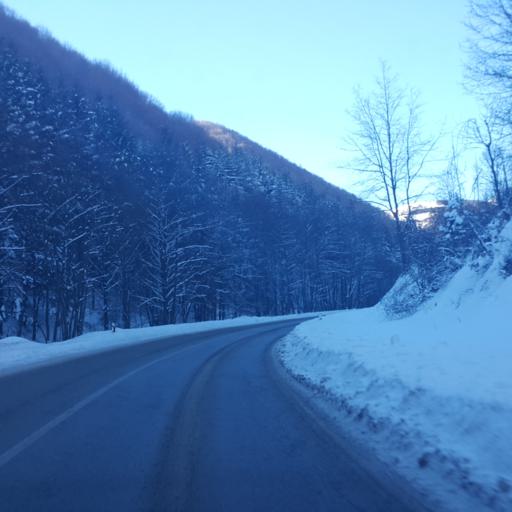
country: RS
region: Central Serbia
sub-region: Rasinski Okrug
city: Aleksandrovac
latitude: 43.3039
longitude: 20.8975
